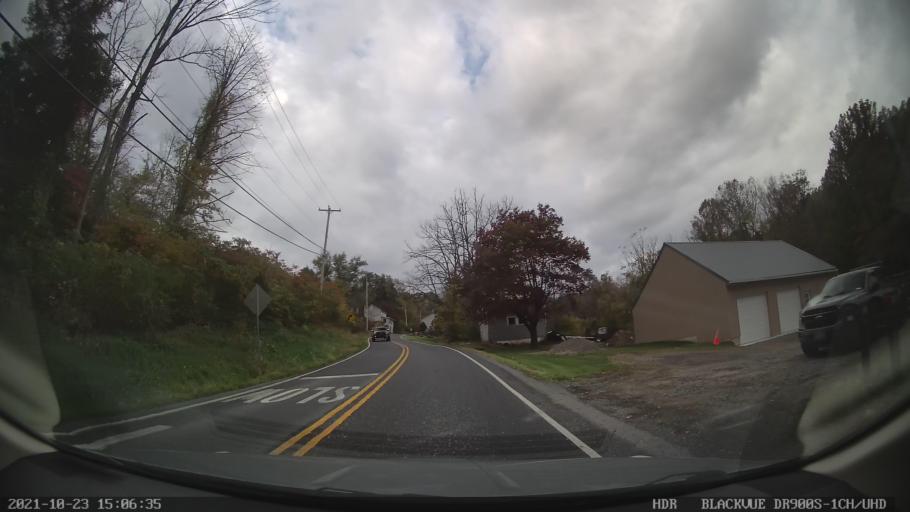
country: US
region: Pennsylvania
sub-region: Berks County
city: Bally
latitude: 40.4350
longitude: -75.5935
